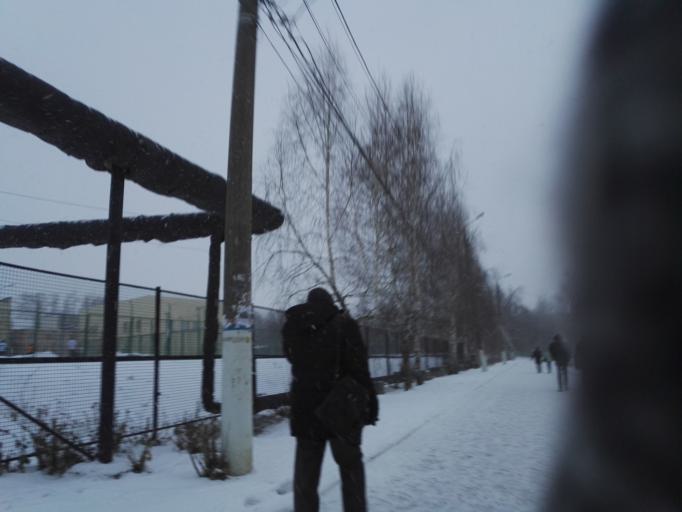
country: RU
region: Tula
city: Mendeleyevskiy
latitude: 54.1726
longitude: 37.5904
